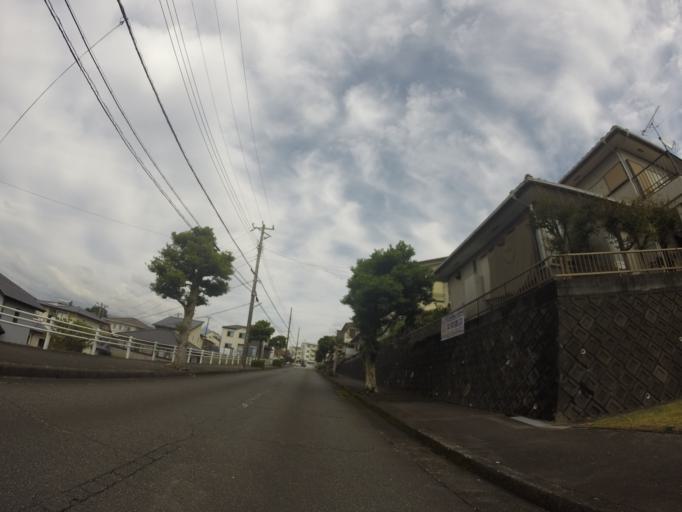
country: JP
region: Shizuoka
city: Fuji
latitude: 35.1836
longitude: 138.7169
